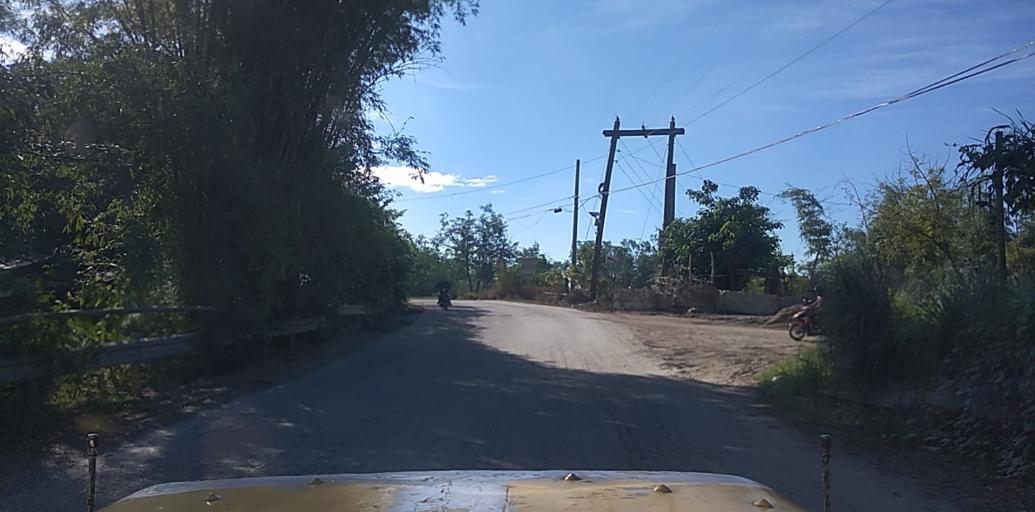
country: PH
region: Central Luzon
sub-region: Province of Pampanga
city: Anao
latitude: 15.1212
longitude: 120.7011
